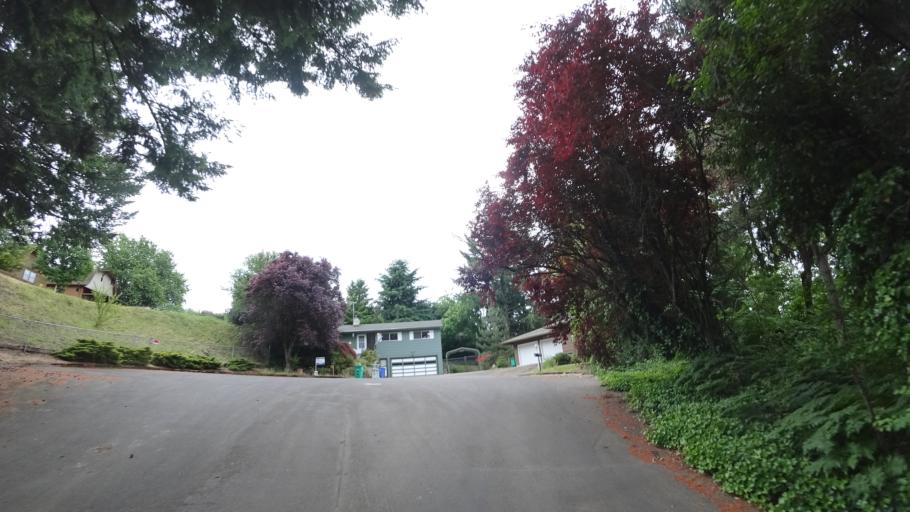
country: US
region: Oregon
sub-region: Clackamas County
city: Happy Valley
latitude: 45.4872
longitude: -122.5224
